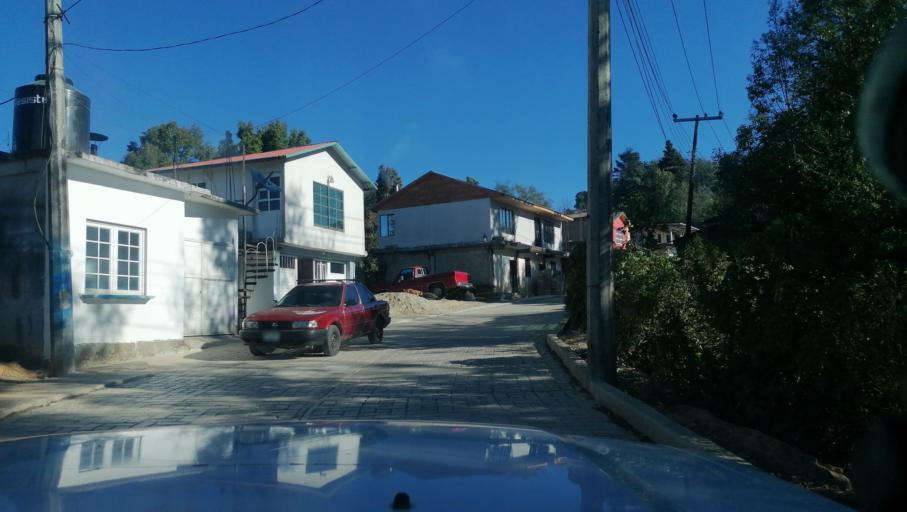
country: MX
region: Chiapas
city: Motozintla de Mendoza
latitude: 15.2568
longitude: -92.2131
